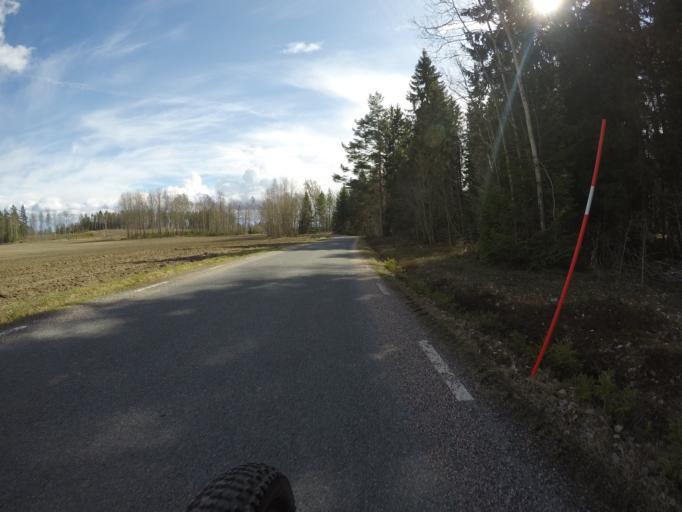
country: SE
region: Vaestmanland
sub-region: Kungsors Kommun
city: Kungsoer
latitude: 59.3140
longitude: 16.1186
